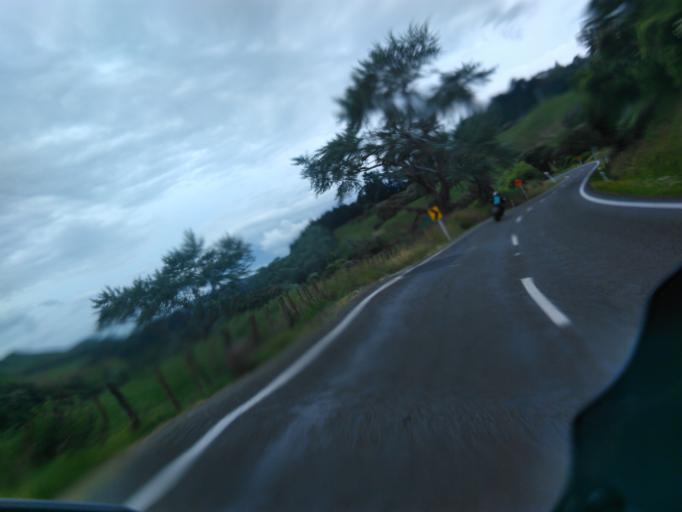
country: NZ
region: Gisborne
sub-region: Gisborne District
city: Gisborne
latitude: -38.4547
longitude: 177.6386
